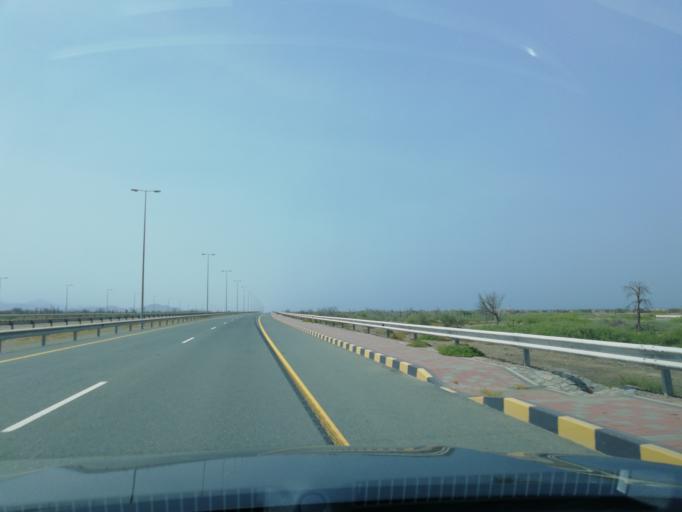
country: OM
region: Al Batinah
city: Shinas
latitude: 24.8762
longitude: 56.4057
